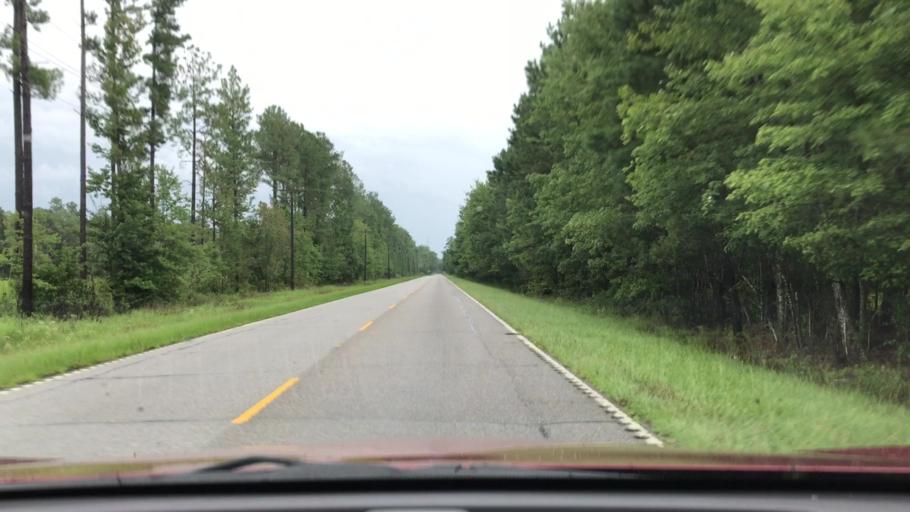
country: US
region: South Carolina
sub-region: Georgetown County
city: Murrells Inlet
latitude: 33.6035
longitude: -79.1996
